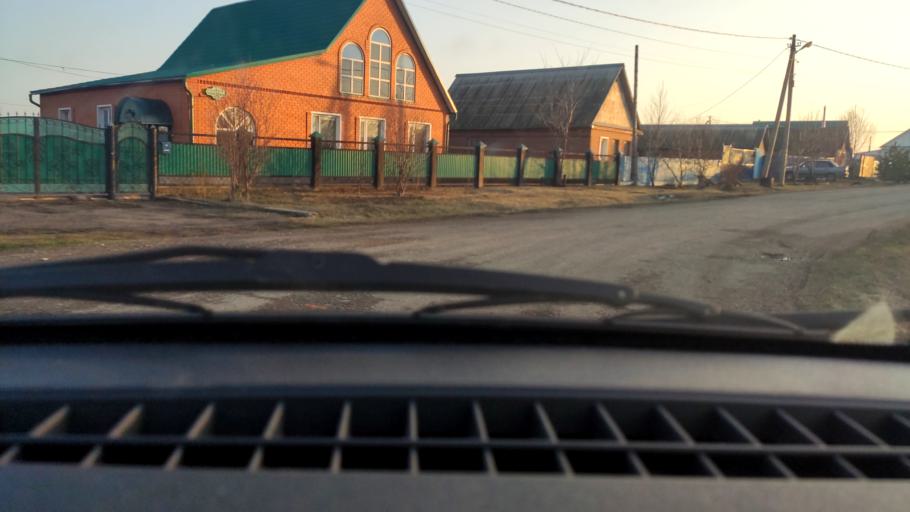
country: RU
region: Bashkortostan
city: Davlekanovo
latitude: 54.2343
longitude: 55.0288
